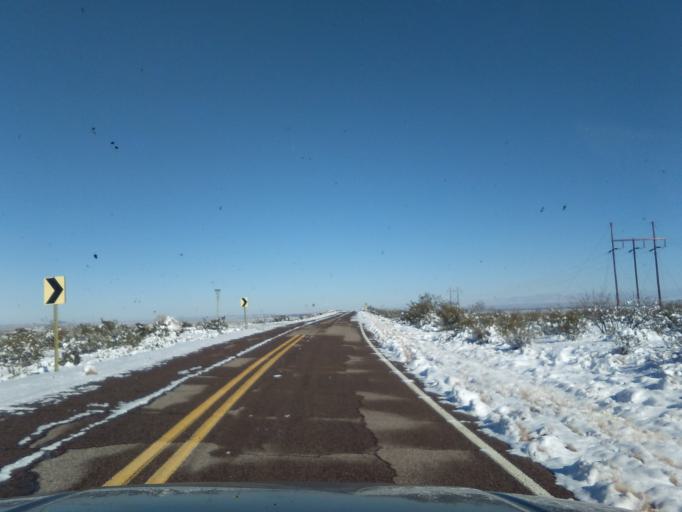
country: US
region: New Mexico
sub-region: Sierra County
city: Elephant Butte
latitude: 33.6060
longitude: -107.1553
